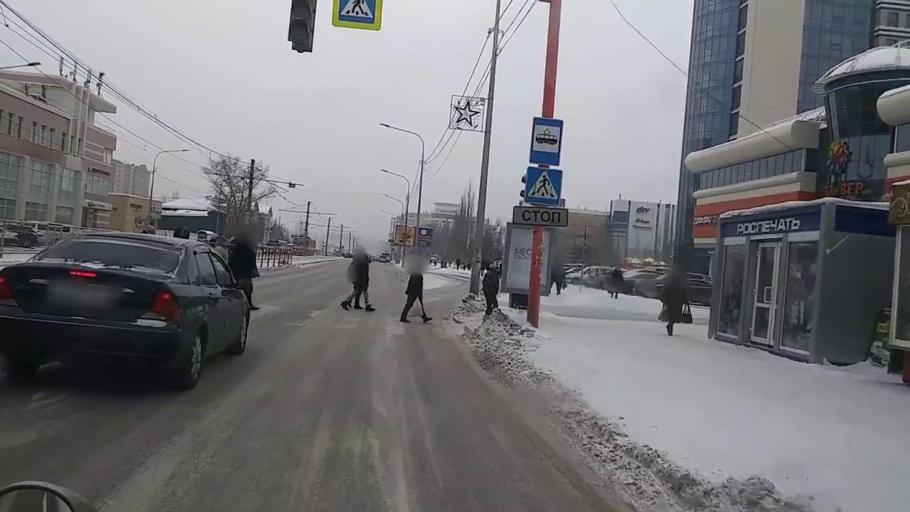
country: RU
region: Altai Krai
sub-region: Gorod Barnaulskiy
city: Barnaul
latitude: 53.3378
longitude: 83.7741
